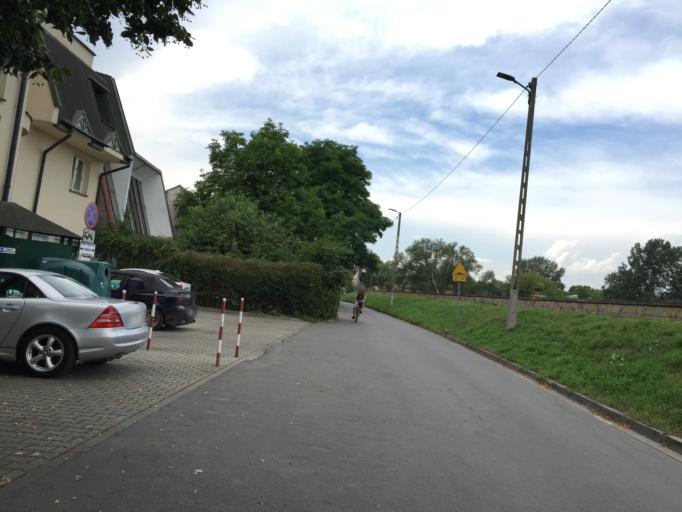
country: PL
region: Lesser Poland Voivodeship
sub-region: Krakow
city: Krakow
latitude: 50.0553
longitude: 19.9108
